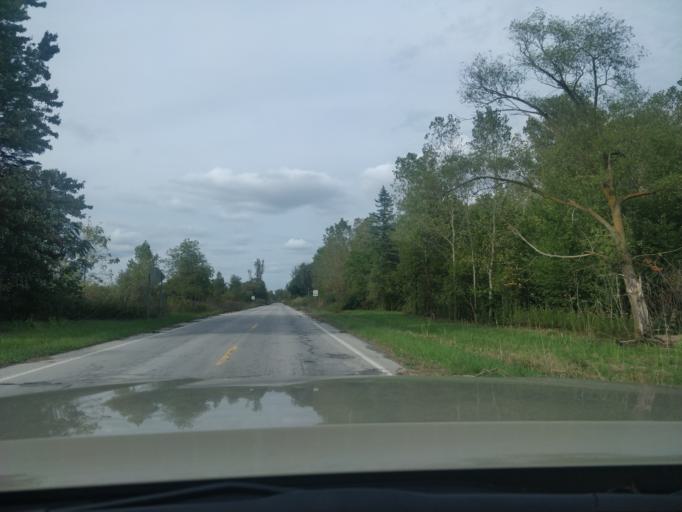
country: US
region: Michigan
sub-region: Wayne County
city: Romulus
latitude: 42.1735
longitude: -83.3643
